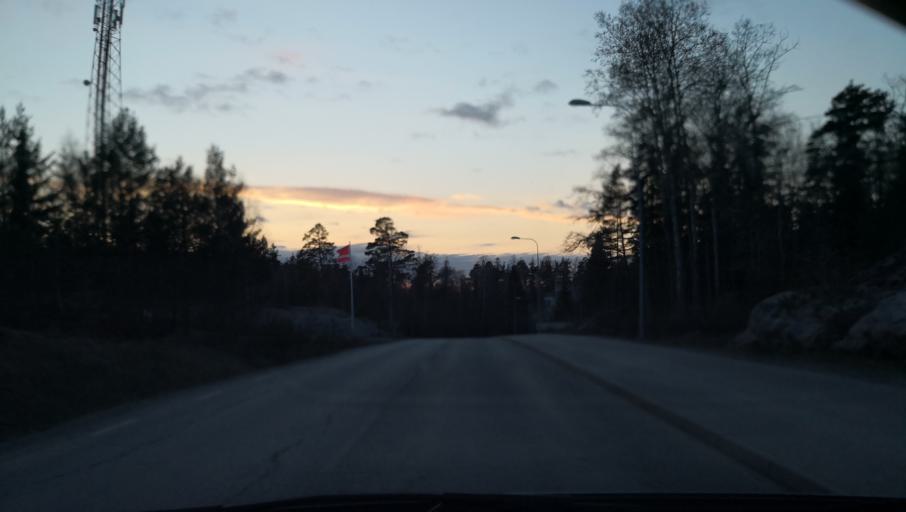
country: SE
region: Stockholm
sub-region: Nacka Kommun
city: Boo
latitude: 59.3414
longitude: 18.2956
